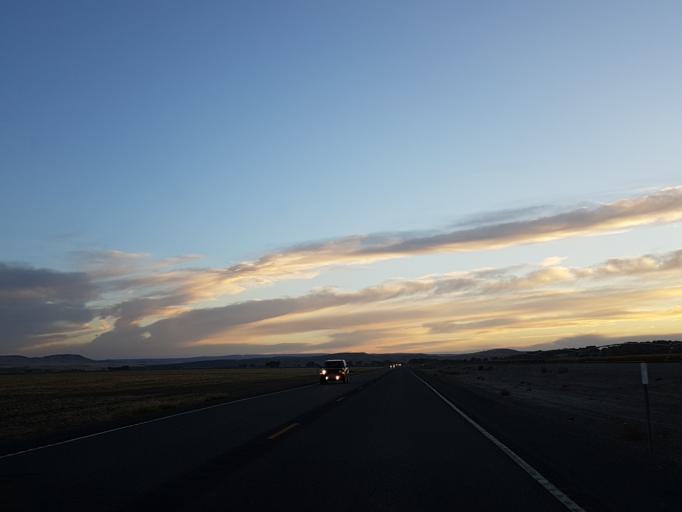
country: US
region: Oregon
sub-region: Malheur County
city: Vale
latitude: 43.9566
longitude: -117.2861
